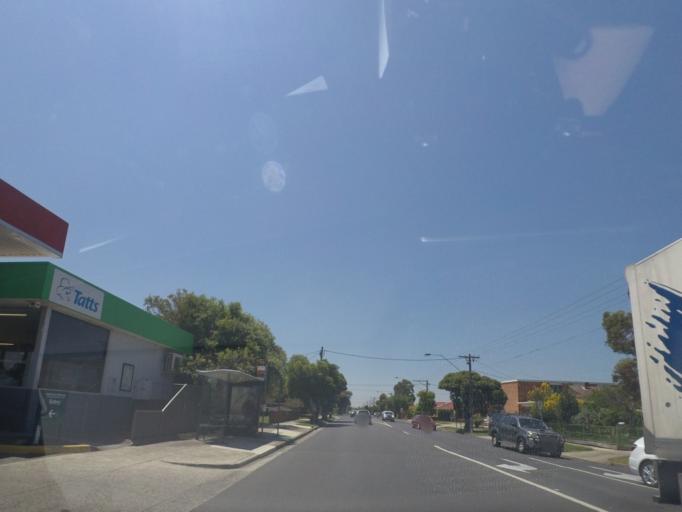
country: AU
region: Victoria
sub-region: Moreland
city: Pascoe Vale
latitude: -37.7378
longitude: 144.9373
